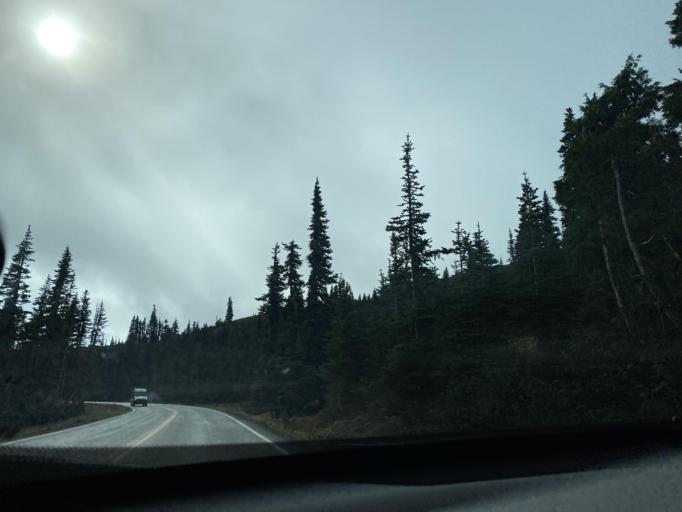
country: US
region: Washington
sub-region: Clallam County
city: Port Angeles
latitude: 47.9723
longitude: -123.4885
